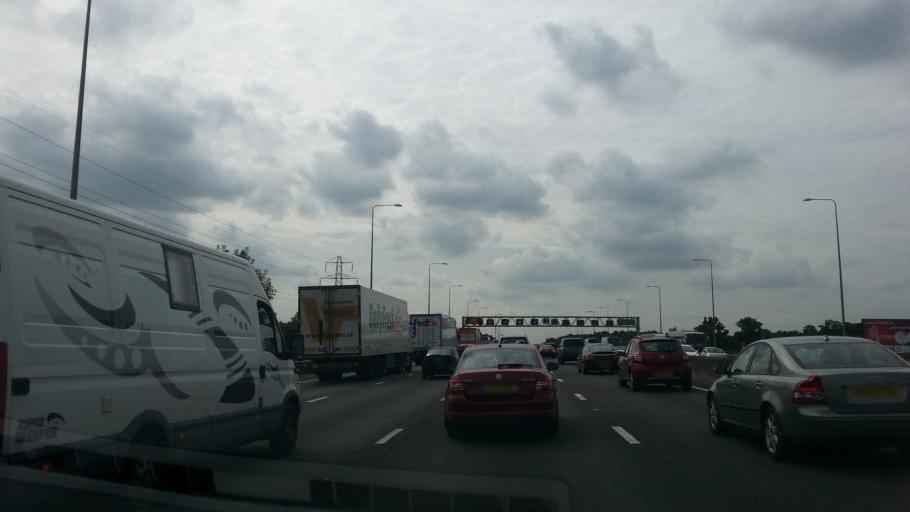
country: GB
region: England
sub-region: Buckinghamshire
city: Chalfont Saint Peter
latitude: 51.6003
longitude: -0.5303
